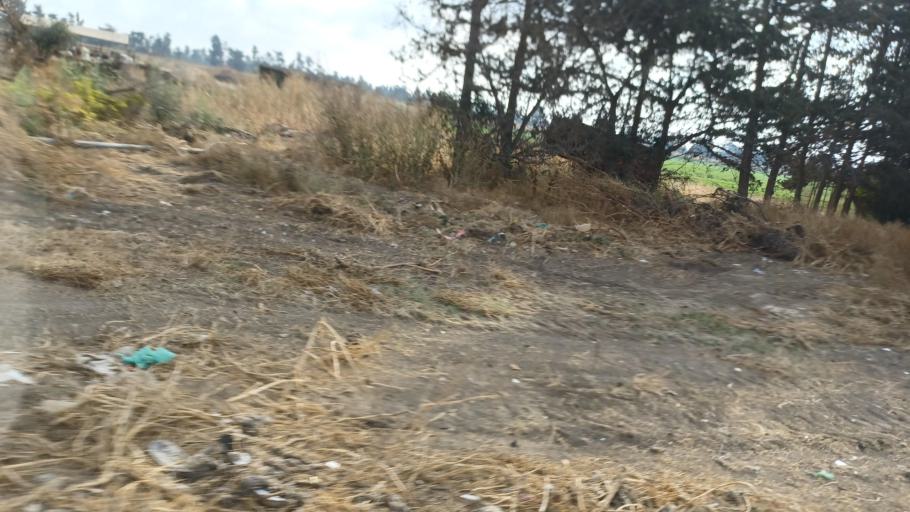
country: CY
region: Larnaka
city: Meneou
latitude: 34.8493
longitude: 33.5957
